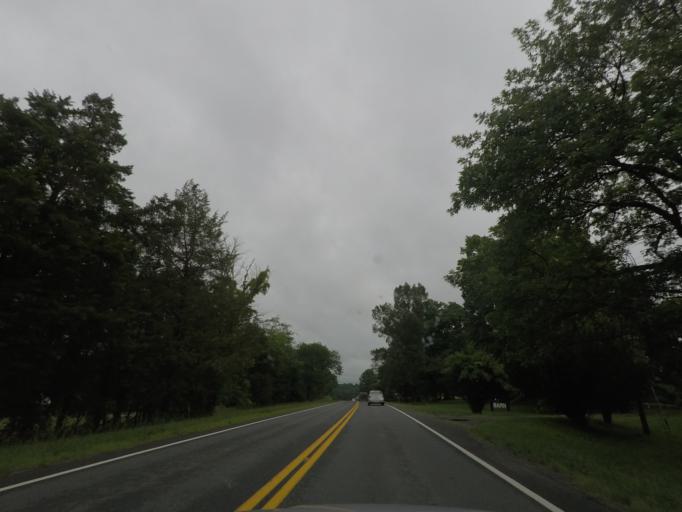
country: US
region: Virginia
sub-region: Fluvanna County
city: Palmyra
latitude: 37.8470
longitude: -78.2719
